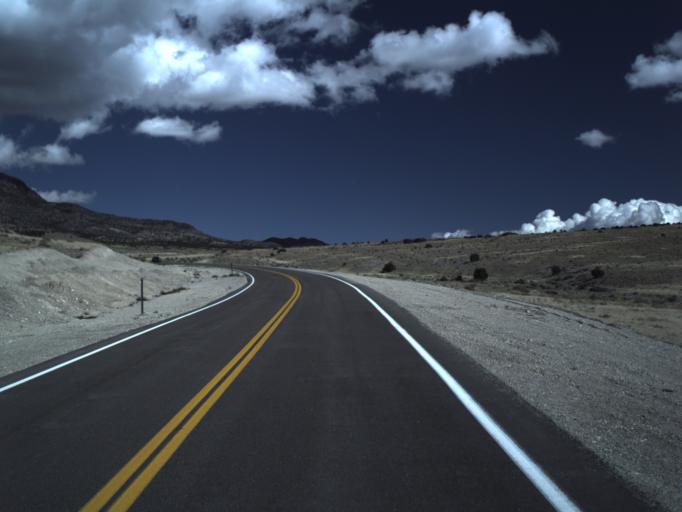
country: US
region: Utah
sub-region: Beaver County
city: Milford
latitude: 38.5064
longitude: -113.5926
